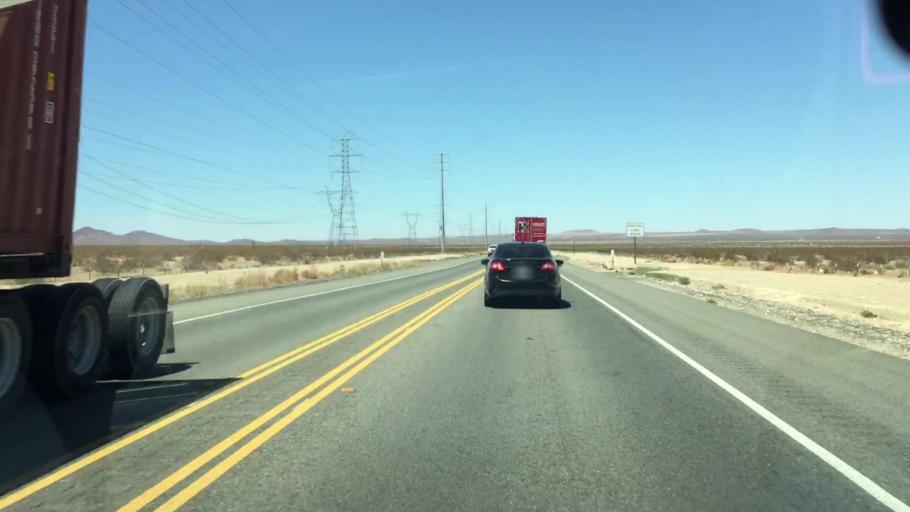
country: US
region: California
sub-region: San Bernardino County
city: Adelanto
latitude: 34.7562
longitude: -117.4724
